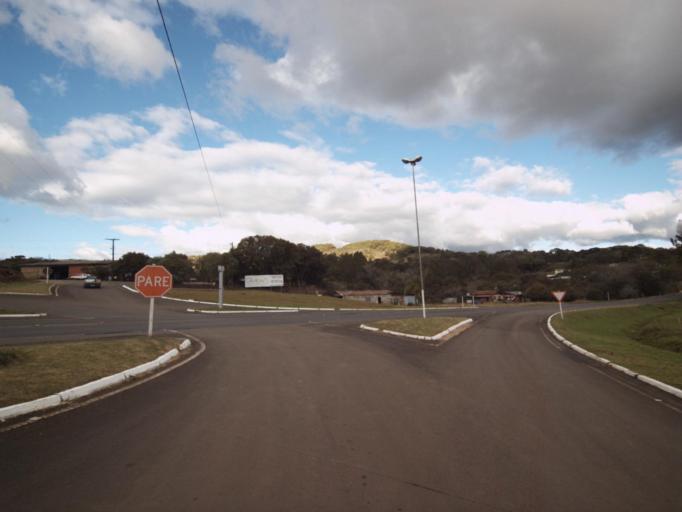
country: BR
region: Santa Catarina
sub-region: Joacaba
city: Joacaba
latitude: -27.2751
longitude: -51.4415
